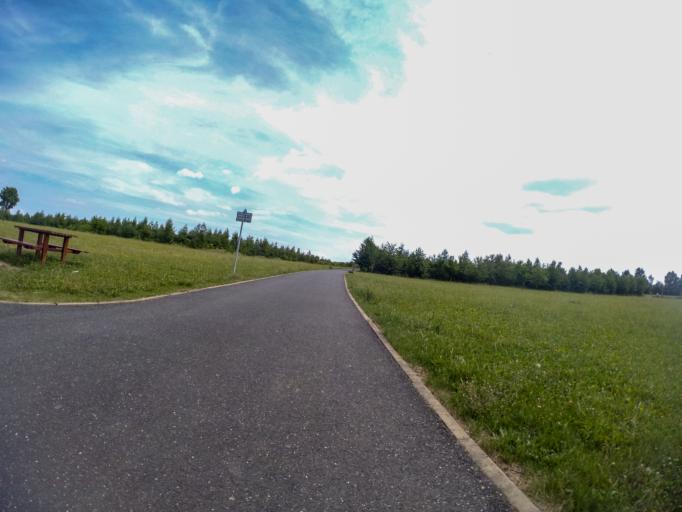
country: CZ
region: Praha
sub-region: Praha 18
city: Letnany
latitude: 50.1369
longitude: 14.5331
